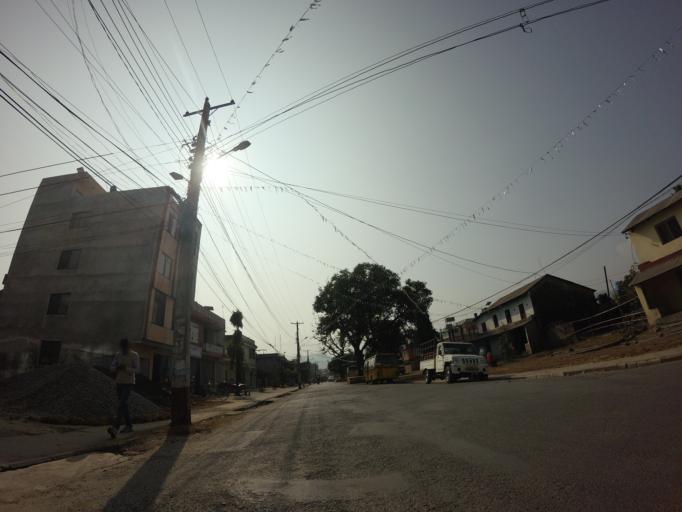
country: NP
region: Western Region
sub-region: Gandaki Zone
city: Pokhara
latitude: 28.2146
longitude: 83.9821
